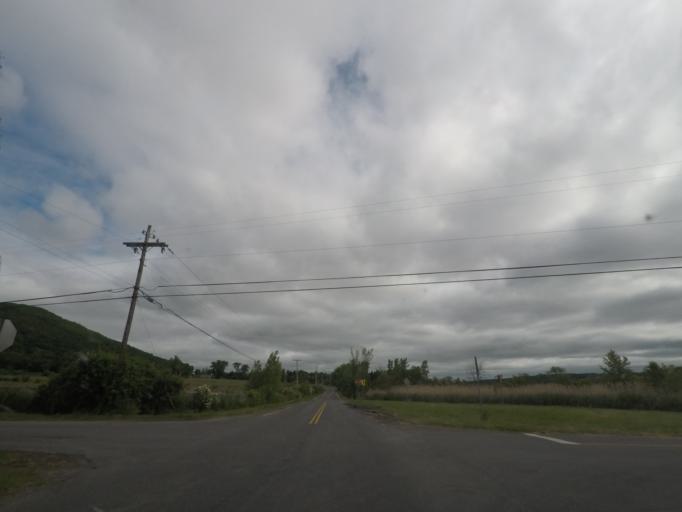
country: US
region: New York
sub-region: Dutchess County
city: Pine Plains
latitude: 41.9937
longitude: -73.5115
